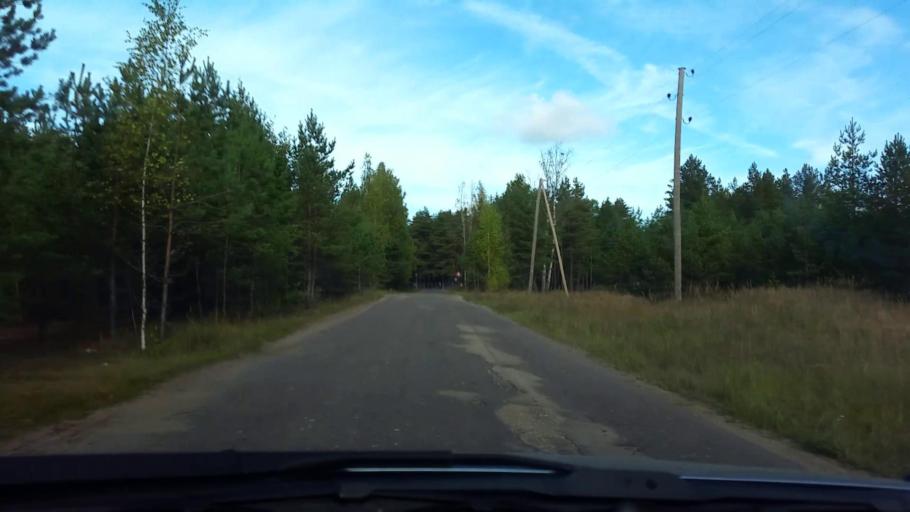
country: LV
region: Adazi
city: Adazi
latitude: 57.1211
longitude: 24.3606
